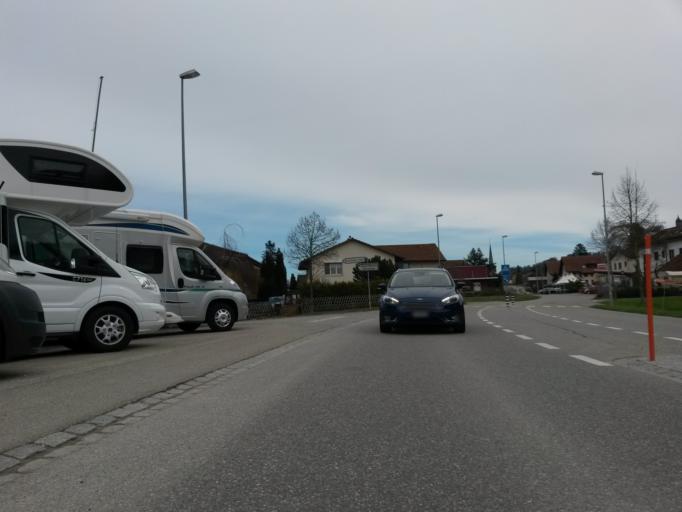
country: CH
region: Bern
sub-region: Seeland District
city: Leuzigen
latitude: 47.1747
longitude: 7.4473
